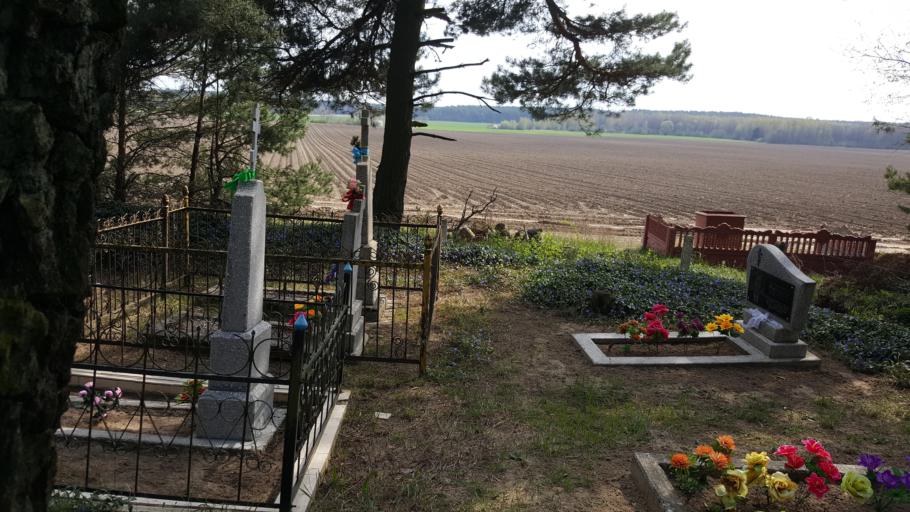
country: BY
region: Brest
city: Zhabinka
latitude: 52.2309
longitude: 23.9119
